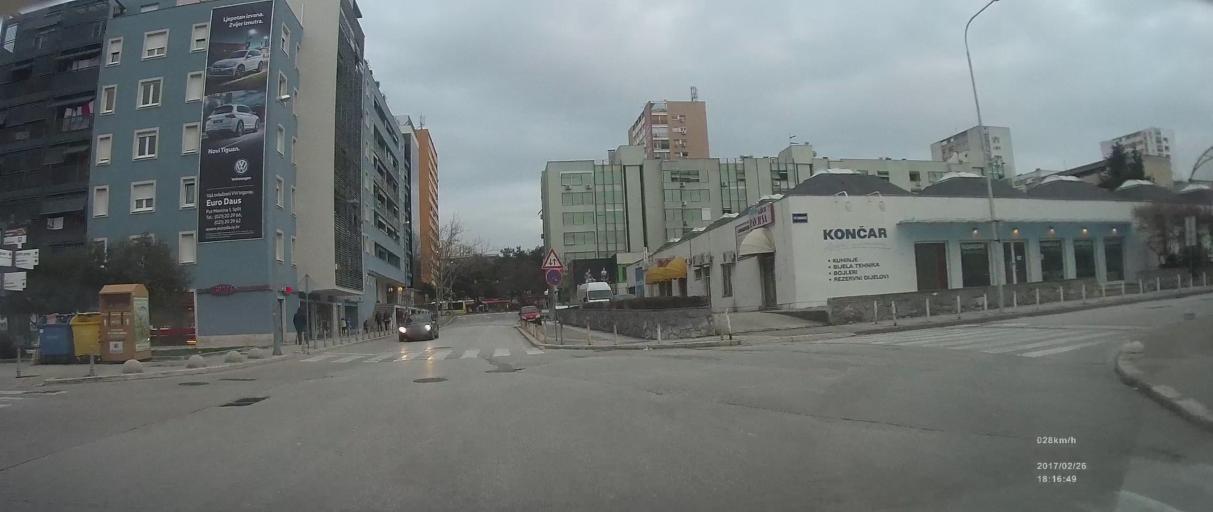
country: HR
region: Splitsko-Dalmatinska
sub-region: Grad Split
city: Split
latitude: 43.5190
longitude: 16.4461
